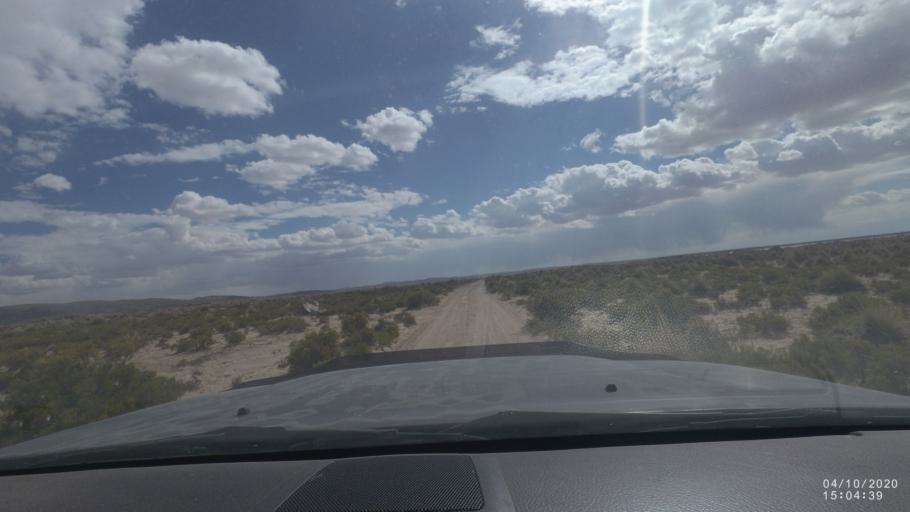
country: BO
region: Oruro
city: Poopo
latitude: -18.6906
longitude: -67.5515
